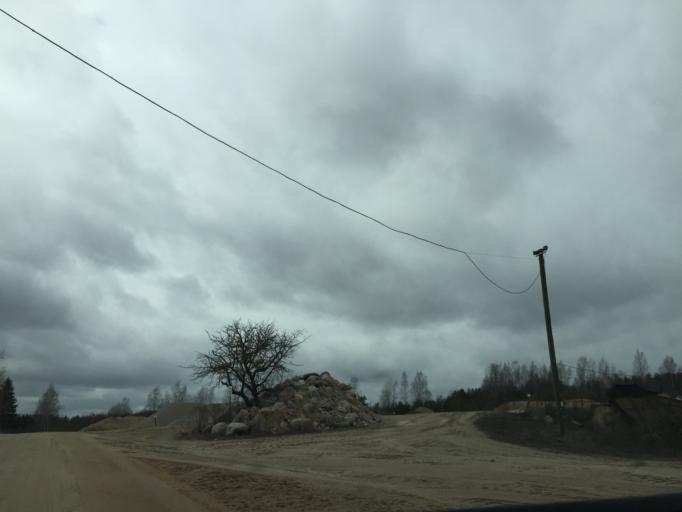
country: LV
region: Aglona
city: Aglona
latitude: 55.9411
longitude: 26.9436
